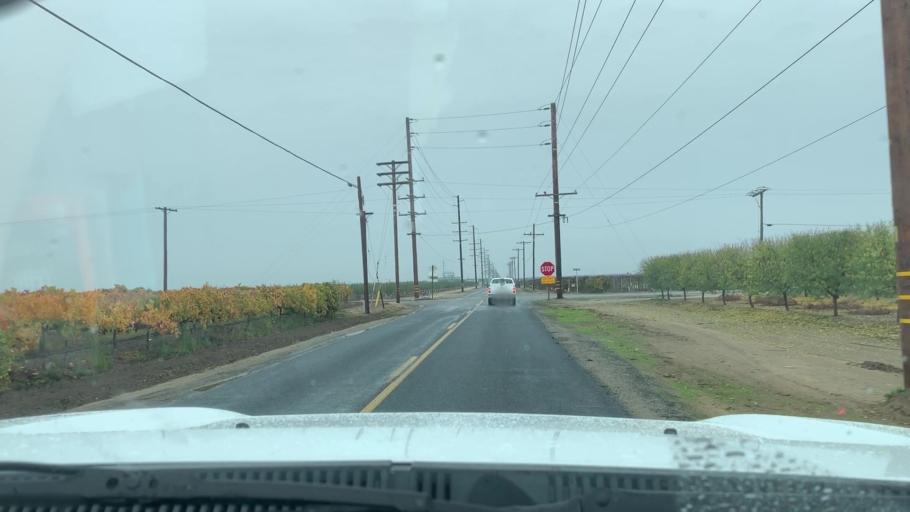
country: US
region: California
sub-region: Kern County
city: Delano
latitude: 35.8340
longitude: -119.2155
